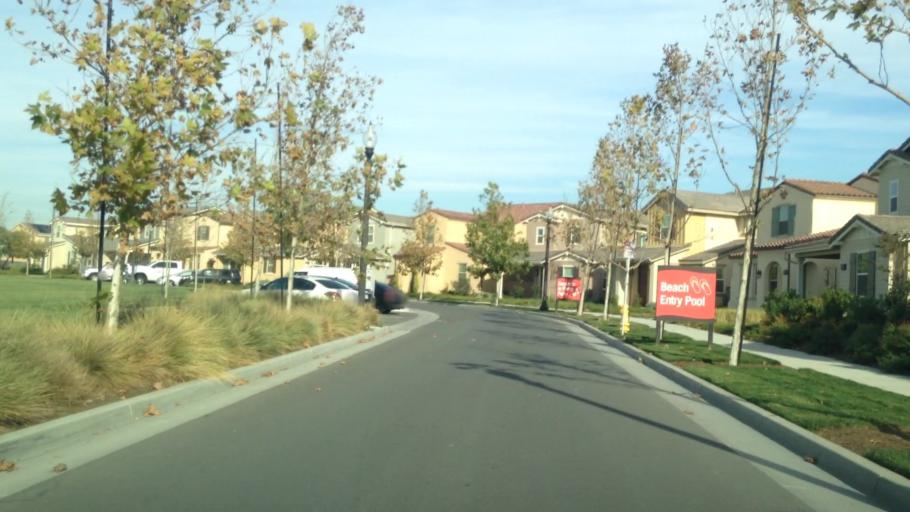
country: US
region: California
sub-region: Riverside County
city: Mira Loma
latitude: 34.0011
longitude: -117.5804
